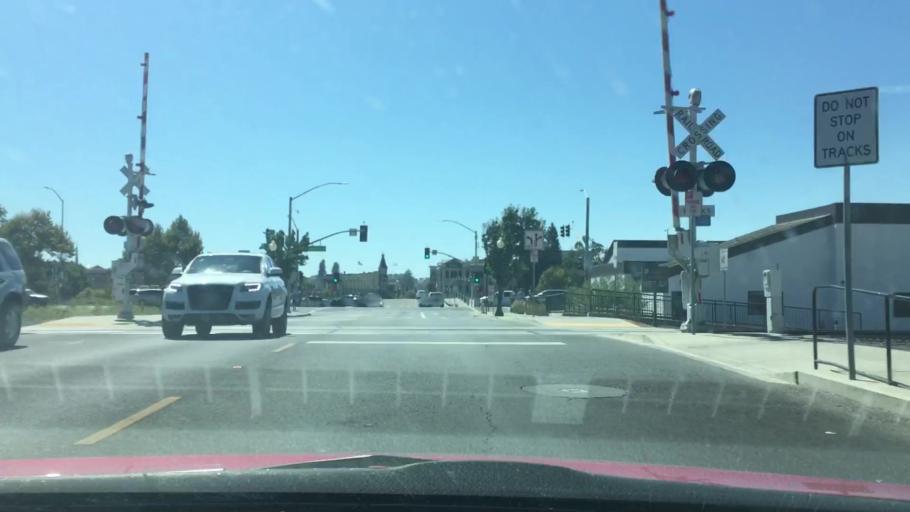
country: US
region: California
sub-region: Napa County
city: Napa
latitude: 38.3007
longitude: -122.2826
